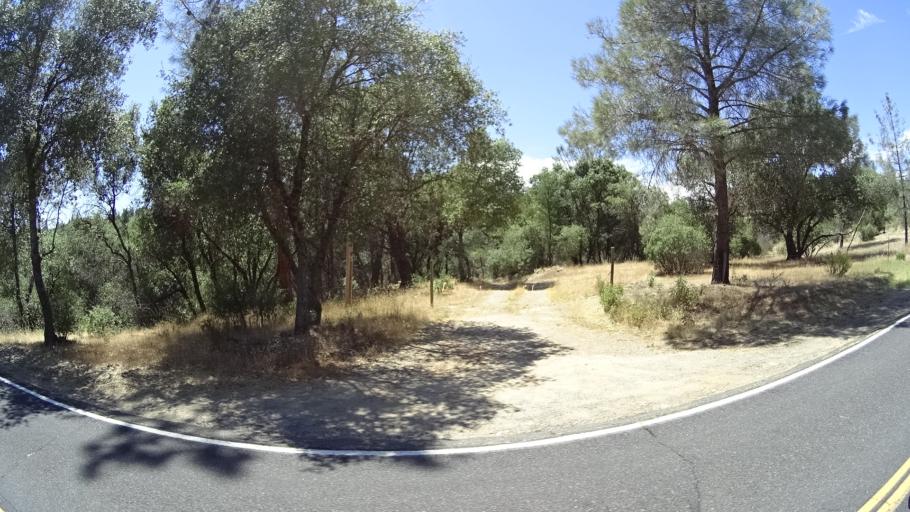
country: US
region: California
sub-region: Calaveras County
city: Mountain Ranch
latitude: 38.2368
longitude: -120.4995
